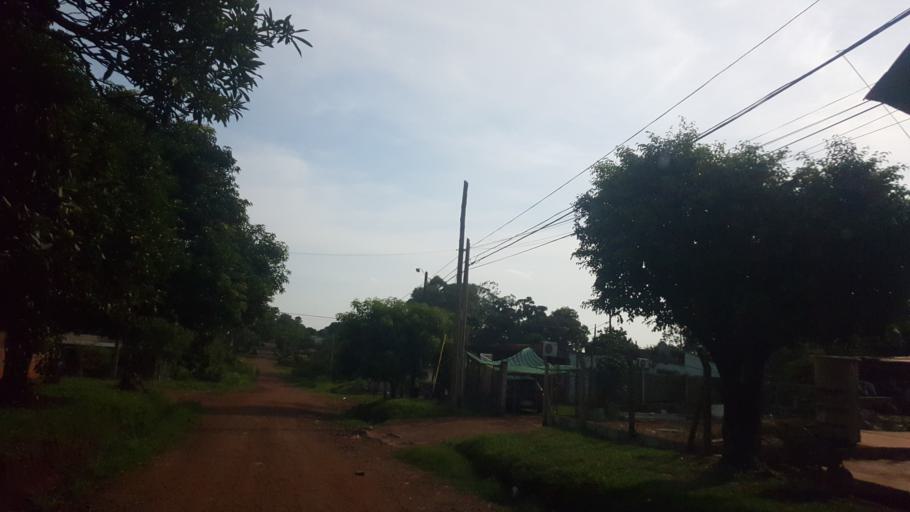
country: AR
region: Misiones
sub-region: Departamento de Capital
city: Posadas
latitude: -27.4032
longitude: -55.9346
